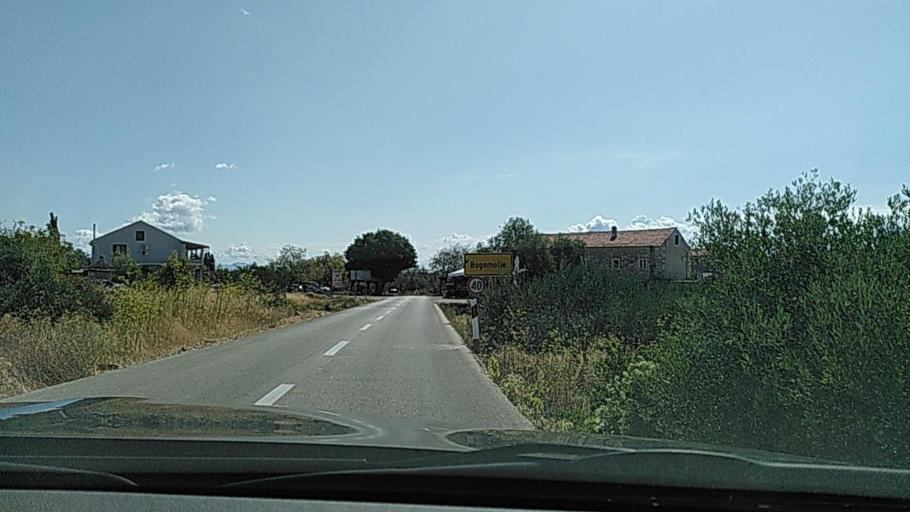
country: HR
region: Splitsko-Dalmatinska
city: Tucepi
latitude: 43.1309
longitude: 16.9828
